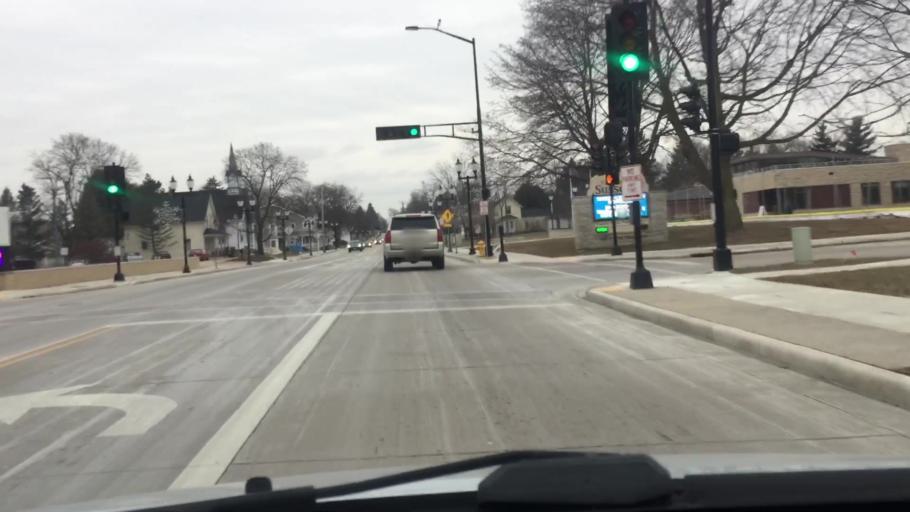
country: US
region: Wisconsin
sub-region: Waukesha County
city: Sussex
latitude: 43.1338
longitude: -88.2190
